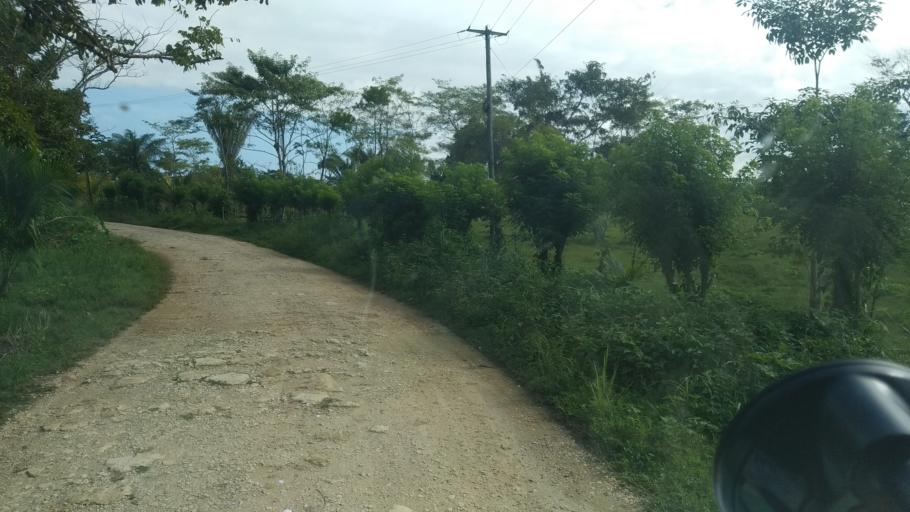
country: BZ
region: Toledo
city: Punta Gorda
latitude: 16.2075
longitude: -88.9141
